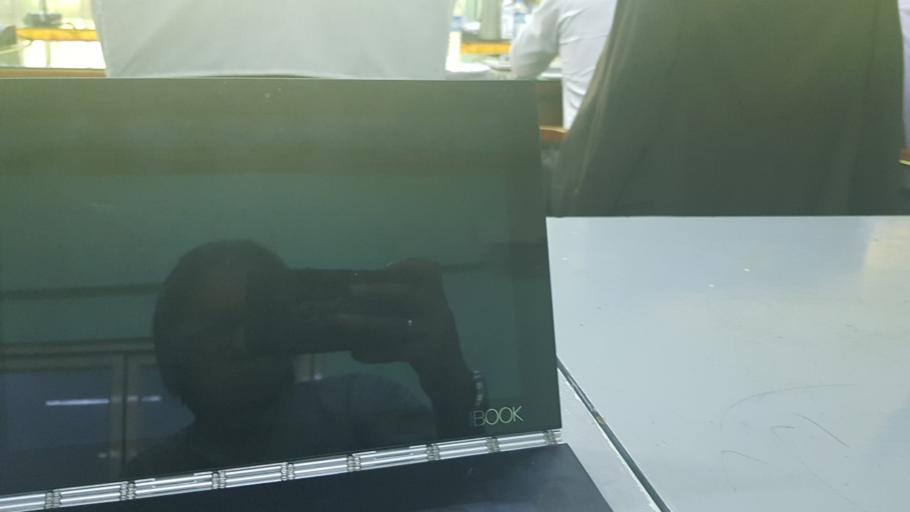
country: MM
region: Mandalay
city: Pyinmana
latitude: 19.8475
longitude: 96.1954
